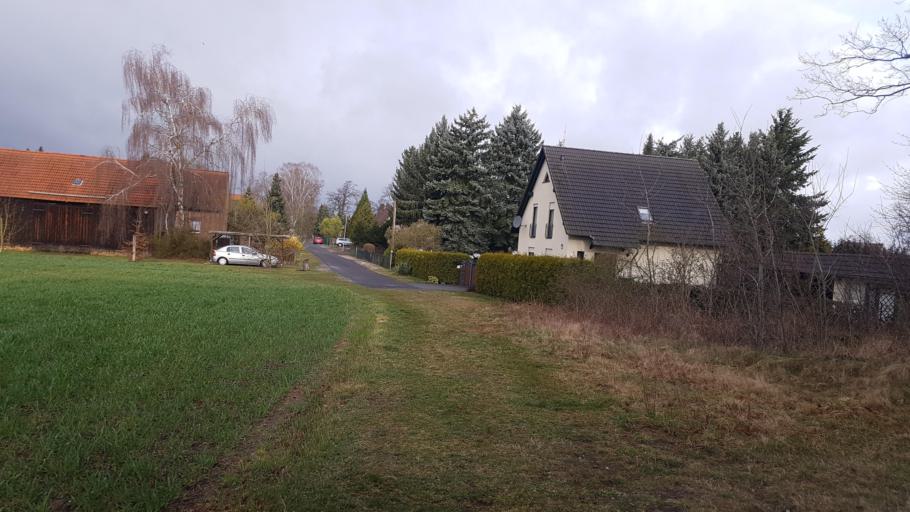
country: DE
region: Brandenburg
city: Bronkow
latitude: 51.6508
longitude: 13.9011
